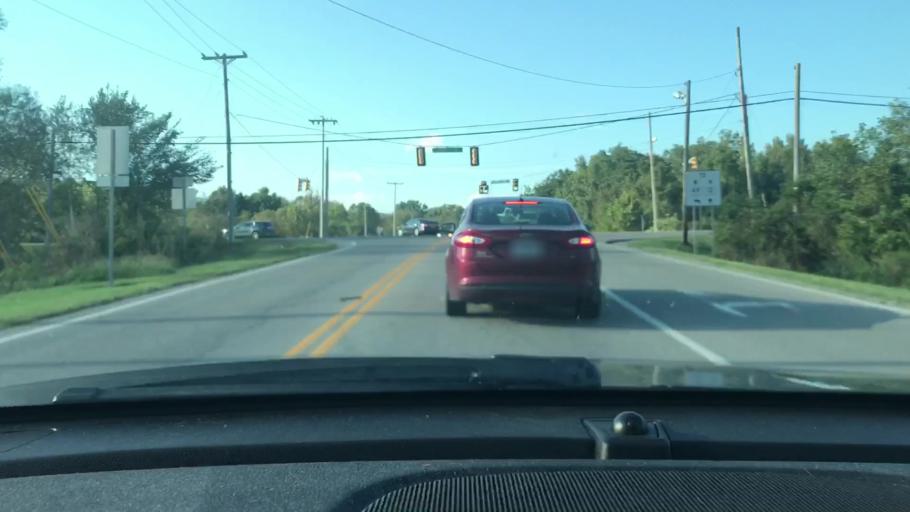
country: US
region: Tennessee
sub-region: Cheatham County
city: Ashland City
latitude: 36.2718
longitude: -87.0696
